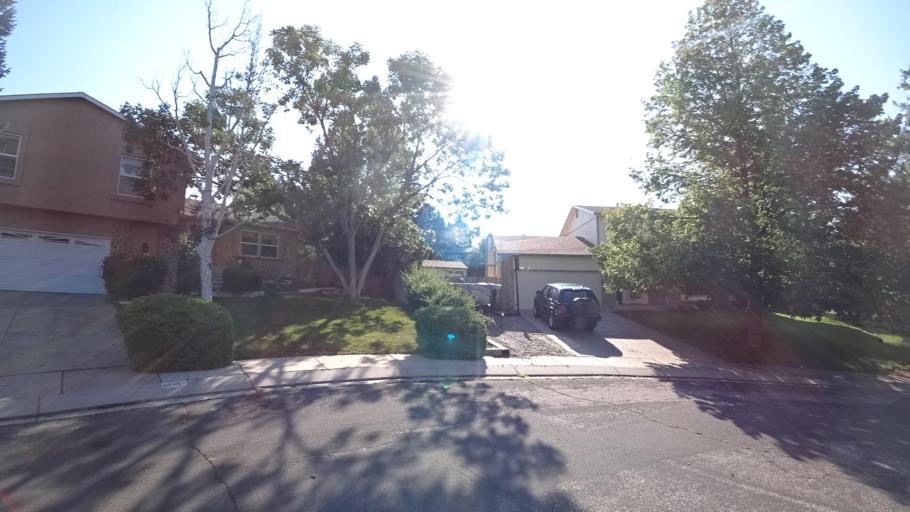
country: US
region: Colorado
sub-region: El Paso County
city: Air Force Academy
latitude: 38.9432
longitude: -104.7781
